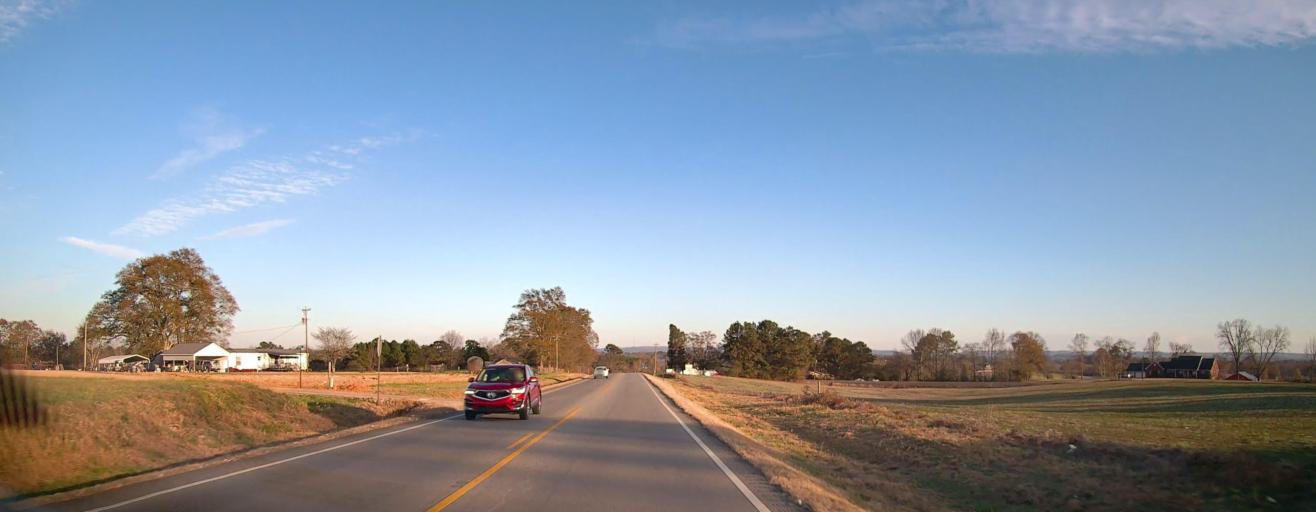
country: US
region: Alabama
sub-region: Blount County
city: Blountsville
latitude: 34.1385
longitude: -86.4361
